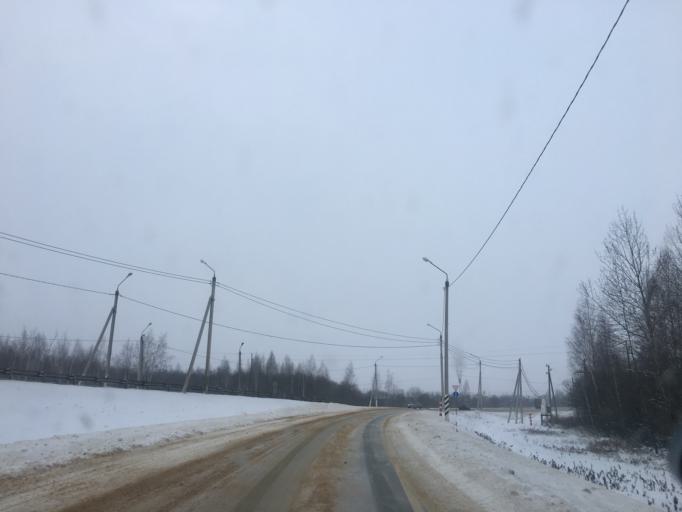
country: RU
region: Tula
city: Kosaya Gora
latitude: 54.1571
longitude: 37.4932
